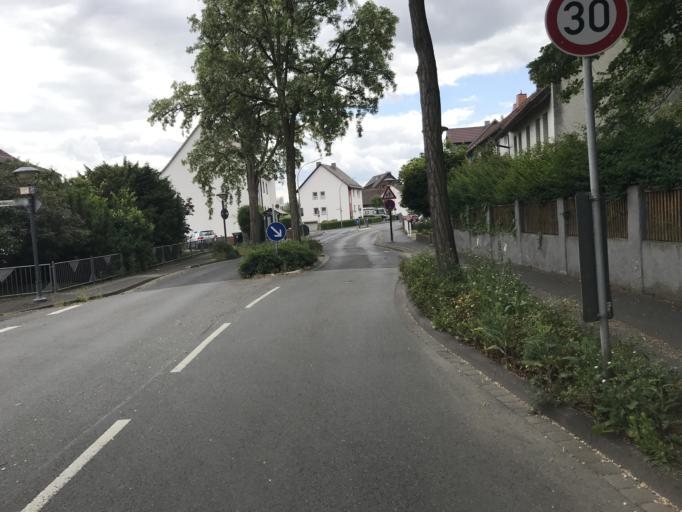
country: DE
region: Hesse
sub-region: Regierungsbezirk Kassel
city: Baunatal
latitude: 51.2516
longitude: 9.3916
